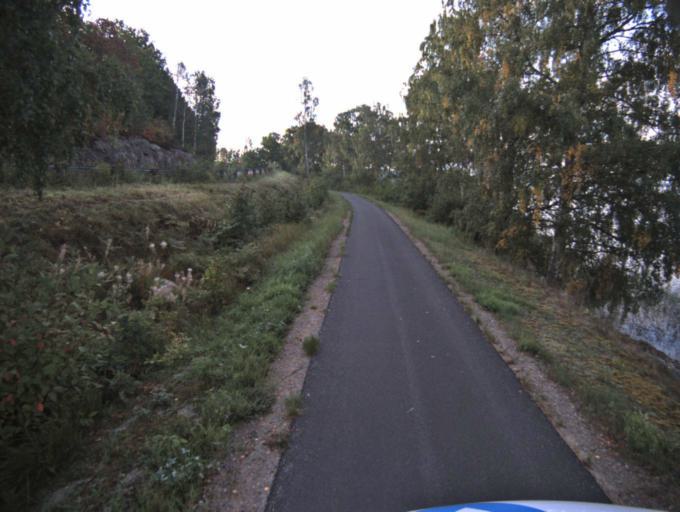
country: SE
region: Vaestra Goetaland
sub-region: Ulricehamns Kommun
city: Ulricehamn
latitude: 57.7447
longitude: 13.3936
